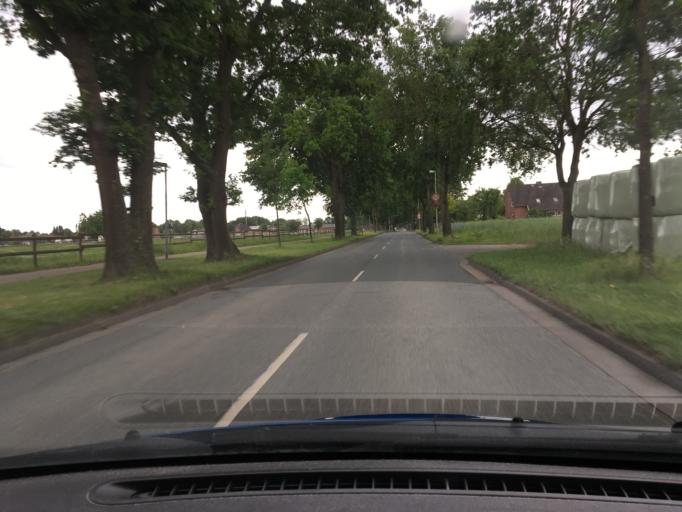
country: DE
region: Lower Saxony
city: Sittensen
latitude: 53.2867
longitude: 9.4999
